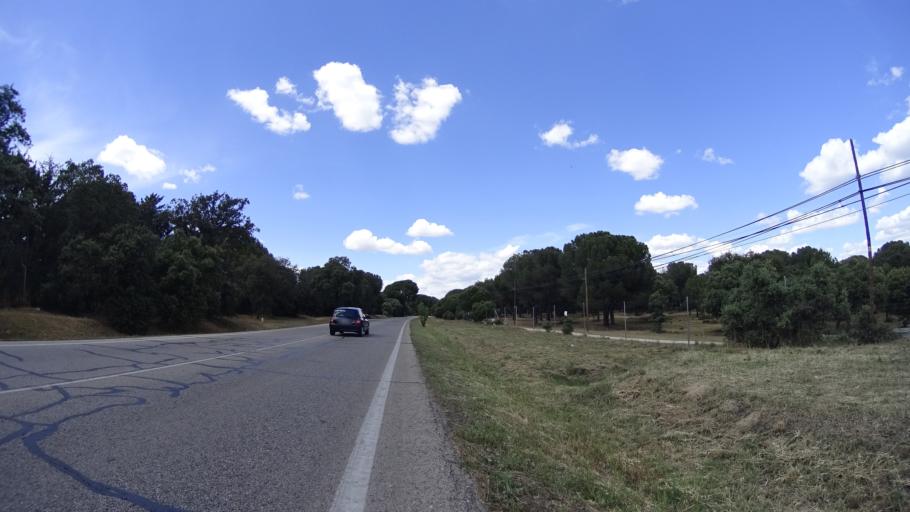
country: ES
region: Madrid
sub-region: Provincia de Madrid
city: Boadilla del Monte
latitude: 40.4305
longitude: -3.8705
